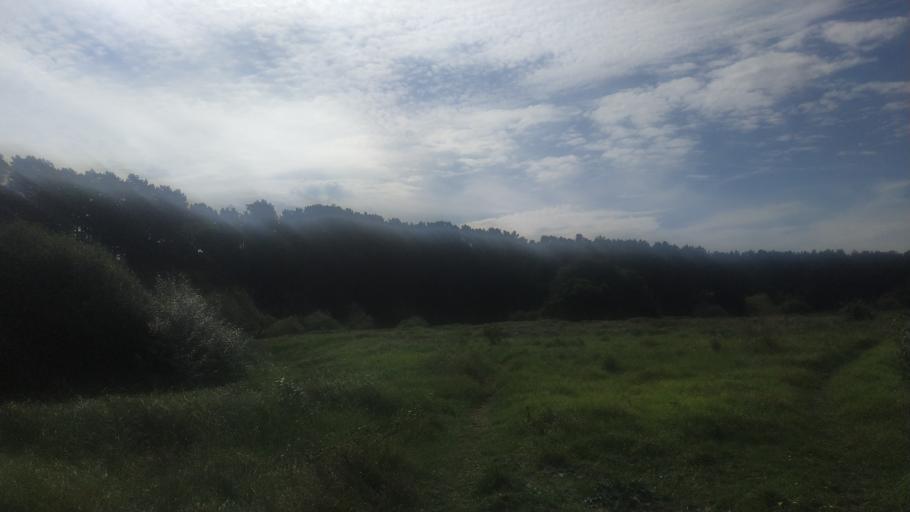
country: RU
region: Brjansk
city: Zhukovka
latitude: 53.5242
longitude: 33.6849
